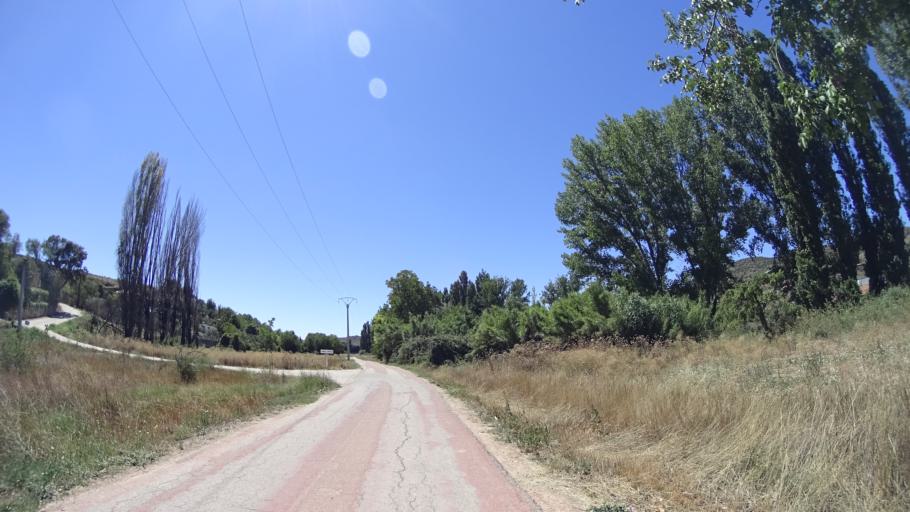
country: ES
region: Madrid
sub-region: Provincia de Madrid
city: Carabana
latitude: 40.2792
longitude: -3.2076
